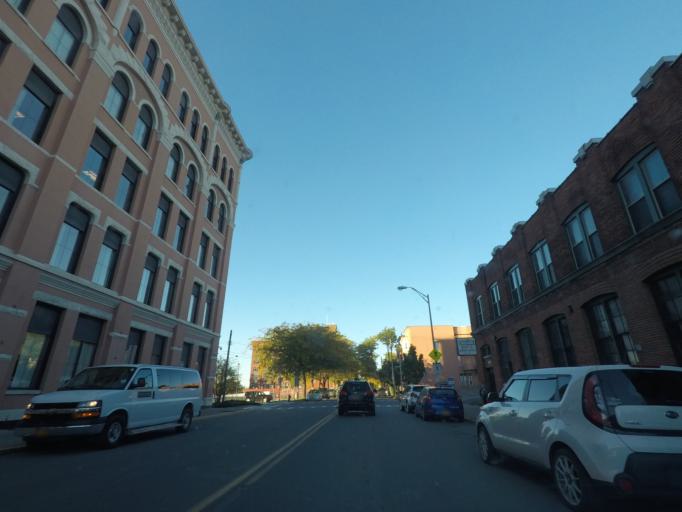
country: US
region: New York
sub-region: Albany County
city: Green Island
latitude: 42.7405
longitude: -73.6857
